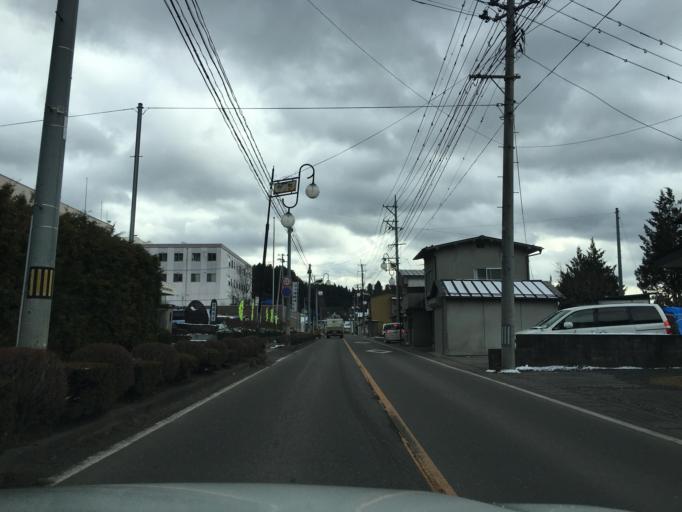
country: JP
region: Fukushima
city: Funehikimachi-funehiki
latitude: 37.2906
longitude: 140.6256
